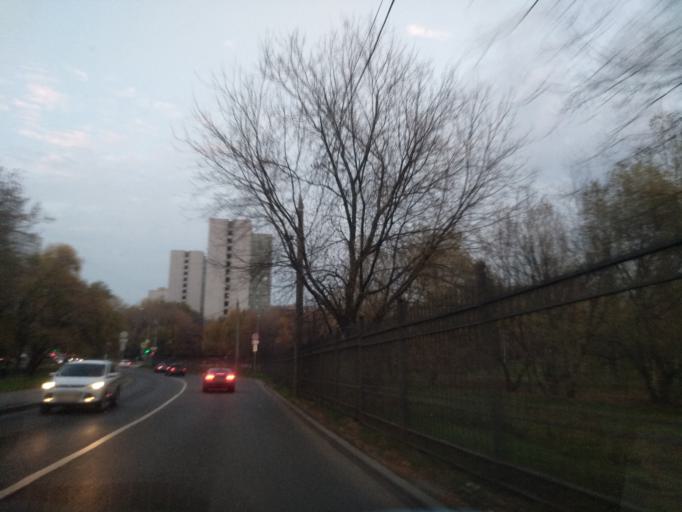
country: RU
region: Moscow
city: Sviblovo
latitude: 55.8658
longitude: 37.6416
